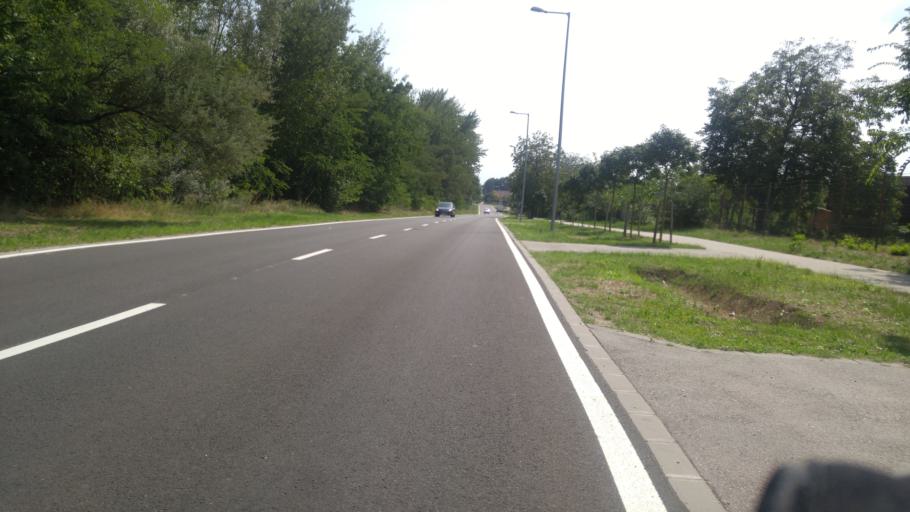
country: HU
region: Budapest
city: Budapest XVII. keruelet
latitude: 47.4575
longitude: 19.2455
